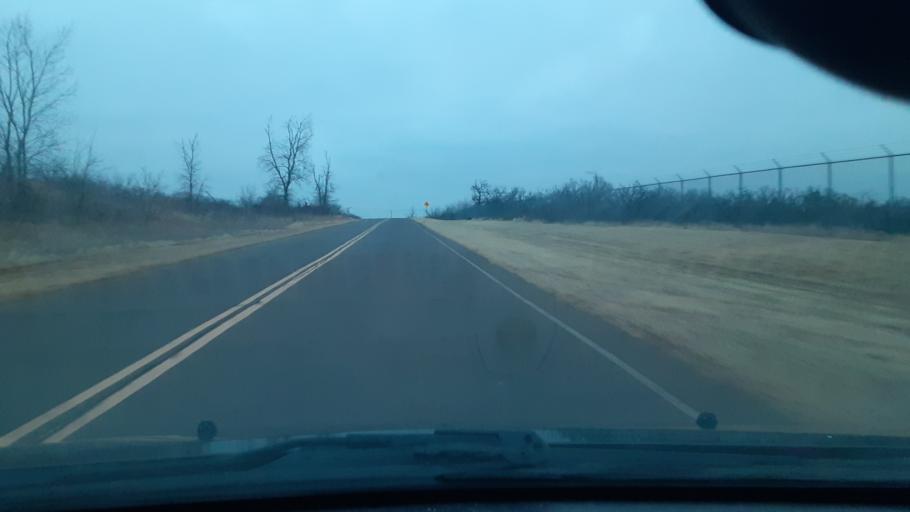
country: US
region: Oklahoma
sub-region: Logan County
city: Guthrie
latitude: 35.8591
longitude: -97.4151
